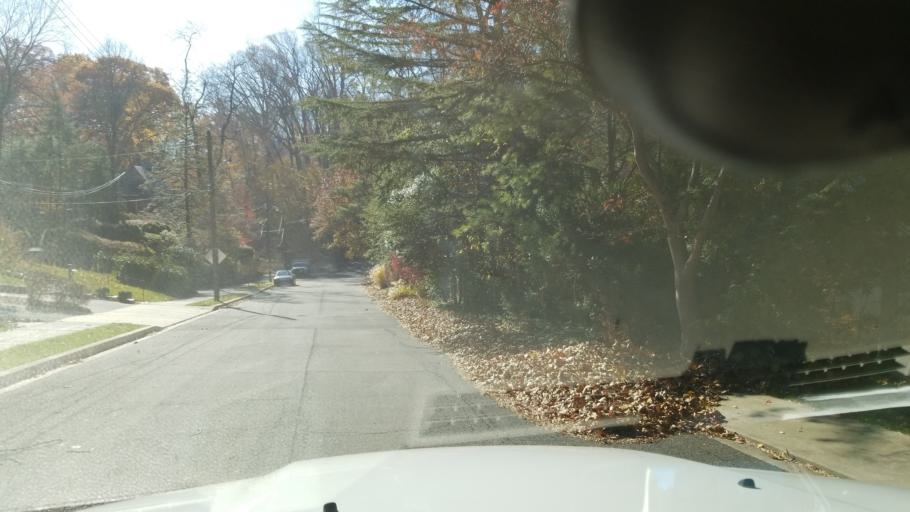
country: US
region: Maryland
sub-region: Montgomery County
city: Friendship Village
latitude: 38.9287
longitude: -77.0838
